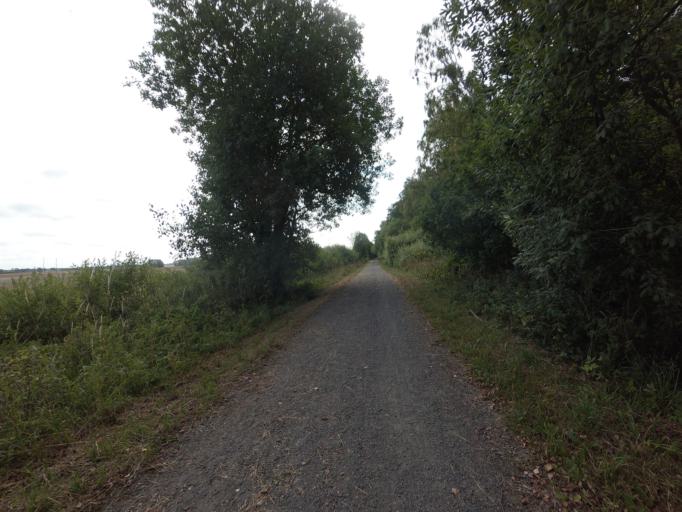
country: SE
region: Skane
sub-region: Helsingborg
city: Odakra
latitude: 56.1729
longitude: 12.6989
